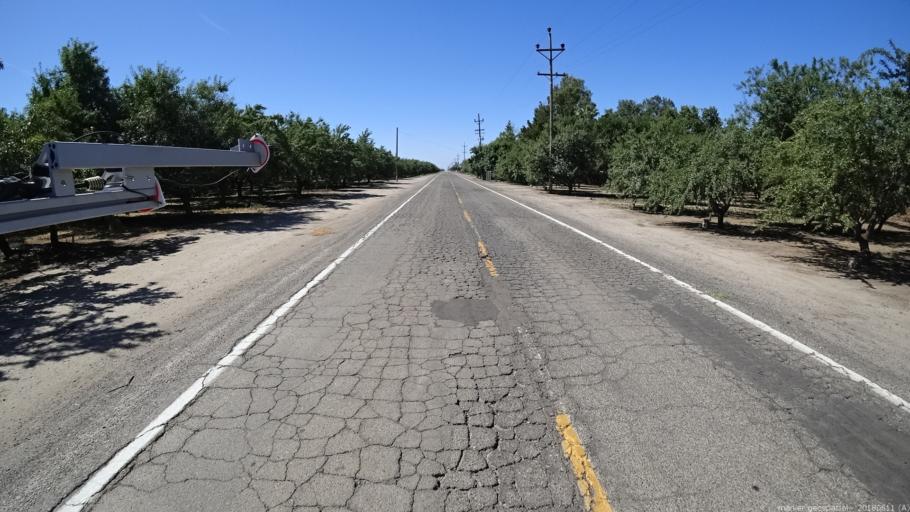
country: US
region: California
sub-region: Madera County
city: Fairmead
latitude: 36.9449
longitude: -120.2018
